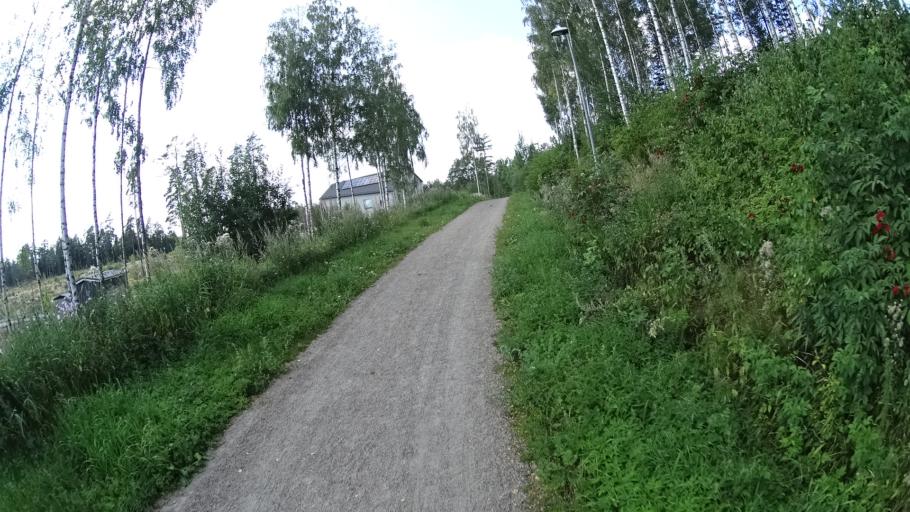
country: FI
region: Uusimaa
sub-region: Porvoo
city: Porvoo
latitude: 60.3786
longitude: 25.7045
